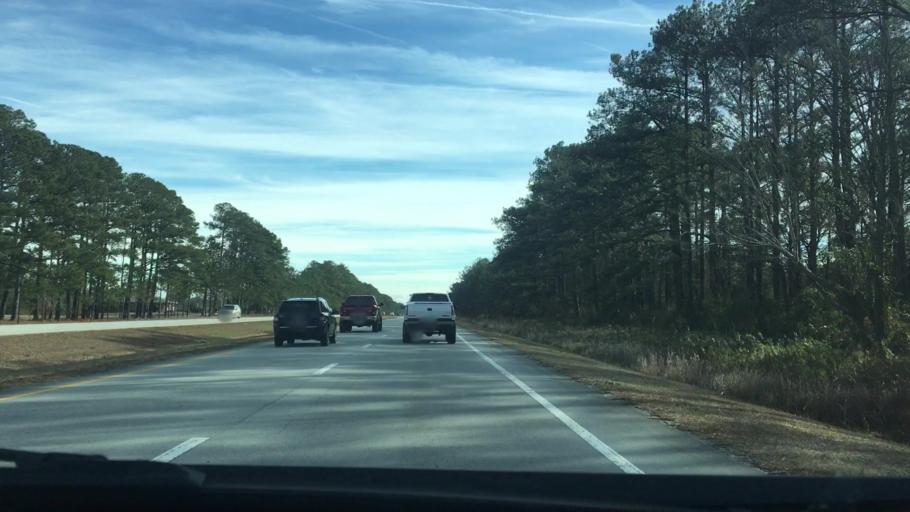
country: US
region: North Carolina
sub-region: Carteret County
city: Newport
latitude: 34.7683
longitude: -76.8626
